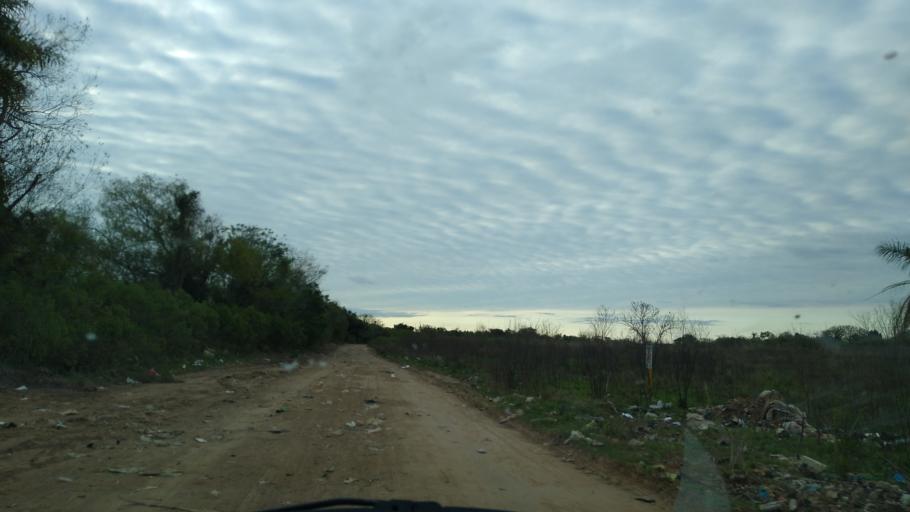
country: AR
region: Chaco
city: Fontana
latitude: -27.3966
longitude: -59.0480
